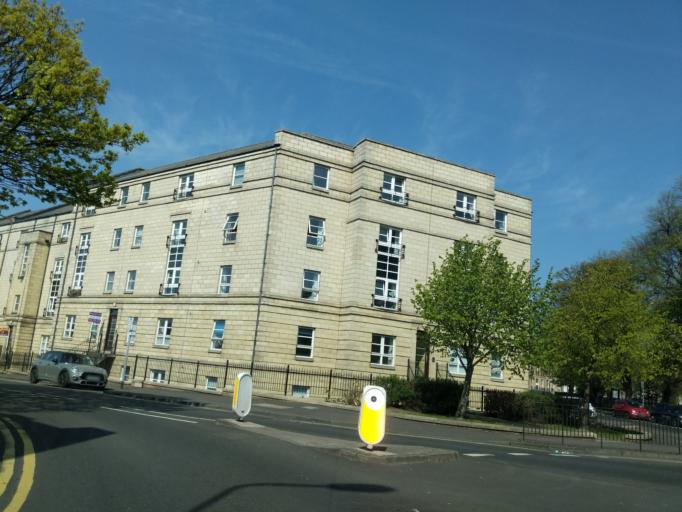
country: GB
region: Scotland
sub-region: Edinburgh
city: Edinburgh
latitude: 55.9605
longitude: -3.1849
